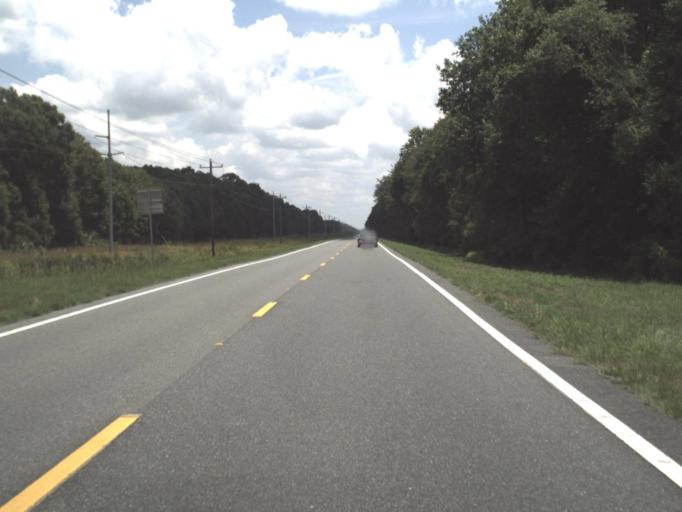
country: US
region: Florida
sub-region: Levy County
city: Chiefland
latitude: 29.2678
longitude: -82.8747
